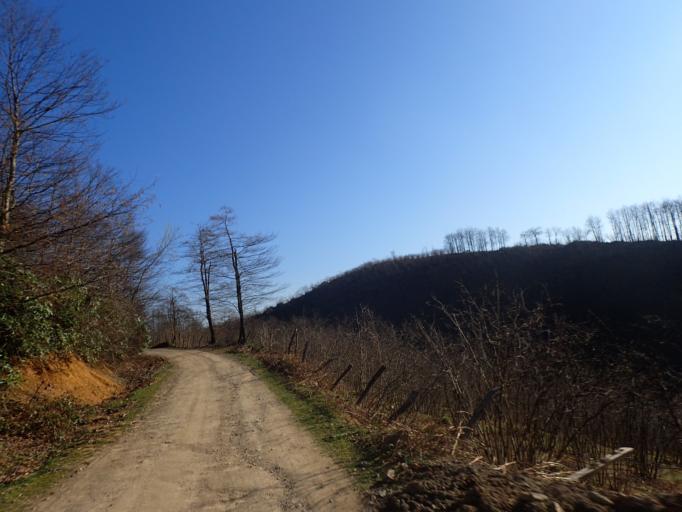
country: TR
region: Ordu
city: Camas
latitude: 40.8555
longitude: 37.5035
